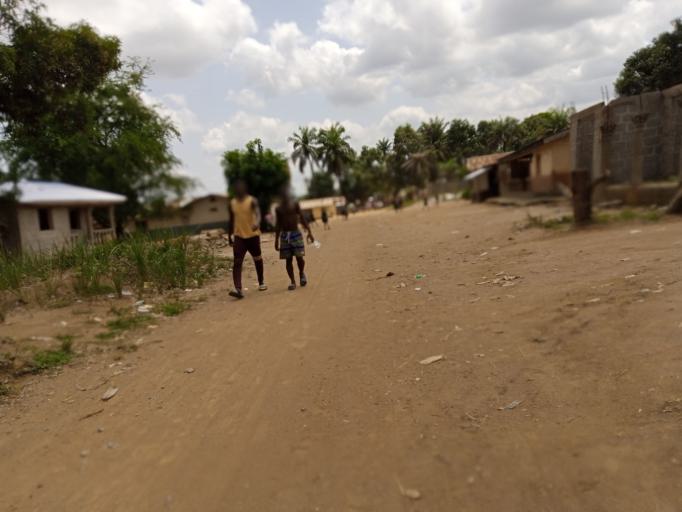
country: SL
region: Western Area
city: Waterloo
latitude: 8.3268
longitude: -13.0143
